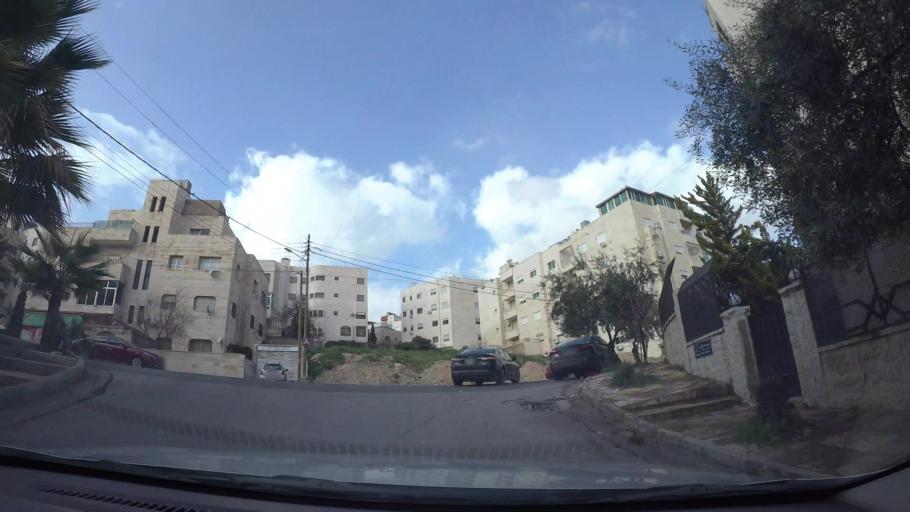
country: JO
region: Amman
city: Al Jubayhah
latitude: 31.9884
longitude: 35.8540
